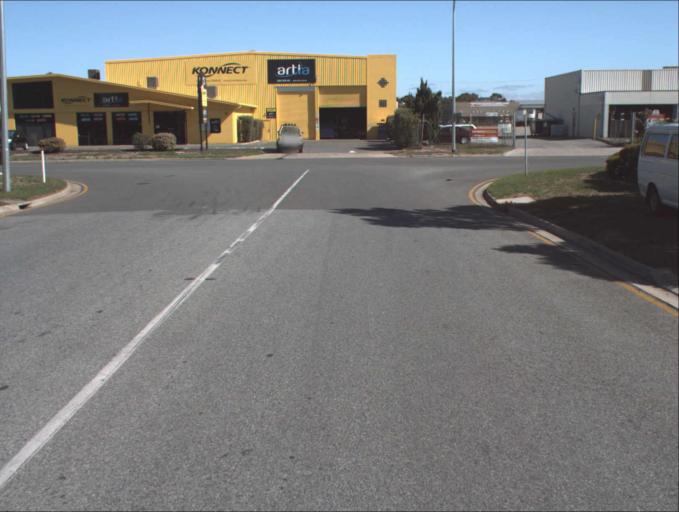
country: AU
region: South Australia
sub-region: Port Adelaide Enfield
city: Blair Athol
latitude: -34.8465
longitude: 138.5678
